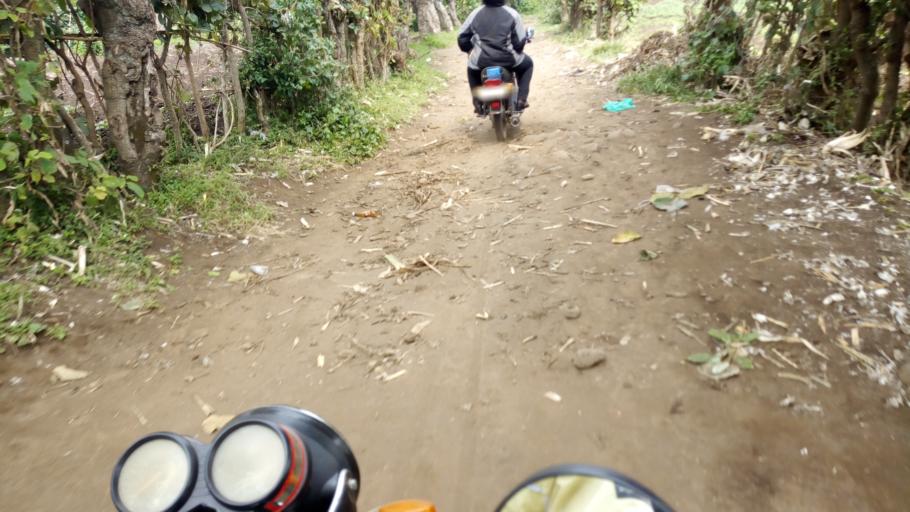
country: UG
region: Western Region
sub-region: Kisoro District
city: Kisoro
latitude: -1.3332
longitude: 29.6069
